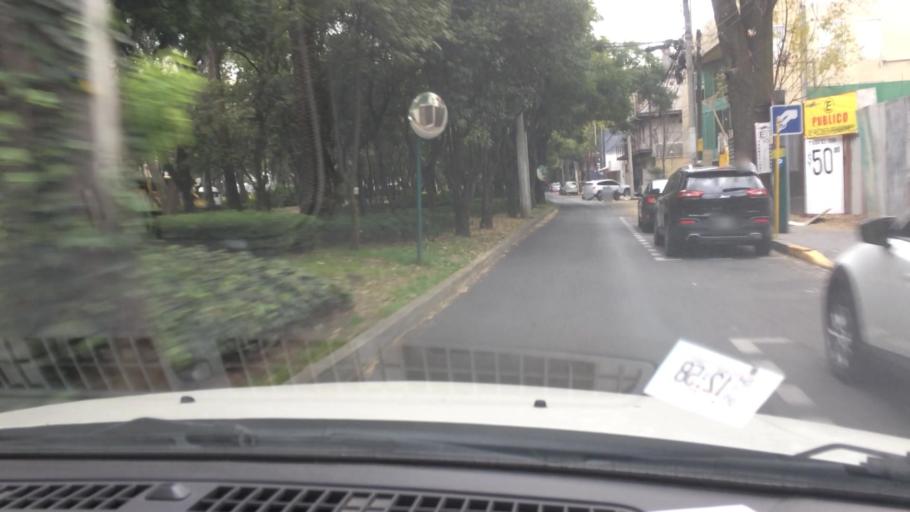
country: MX
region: Mexico City
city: Coyoacan
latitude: 19.3518
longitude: -99.1813
